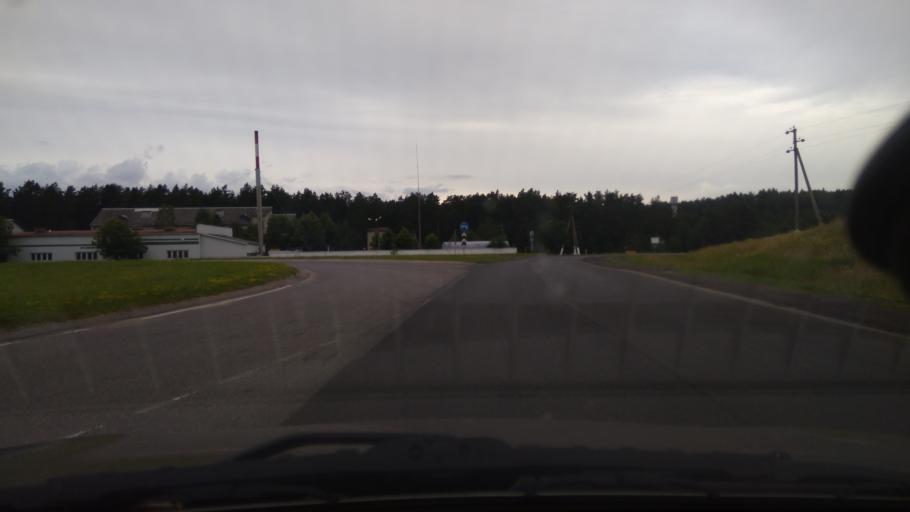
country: BY
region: Minsk
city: Rakaw
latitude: 53.9794
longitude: 27.0420
